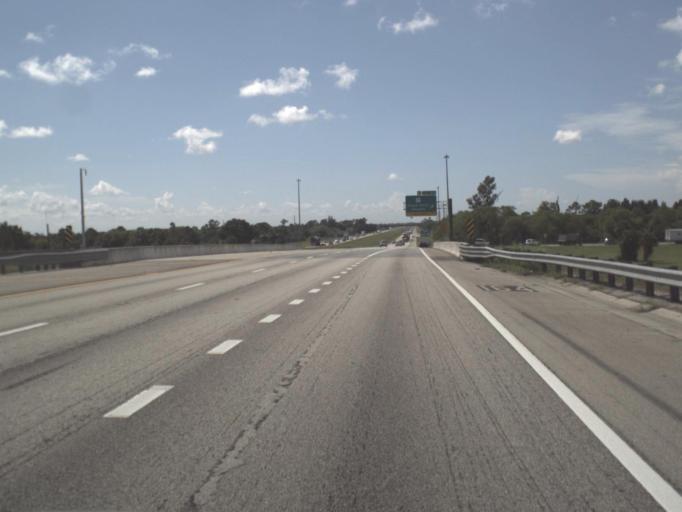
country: US
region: Florida
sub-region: Charlotte County
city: Punta Gorda
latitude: 26.9414
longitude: -82.0195
